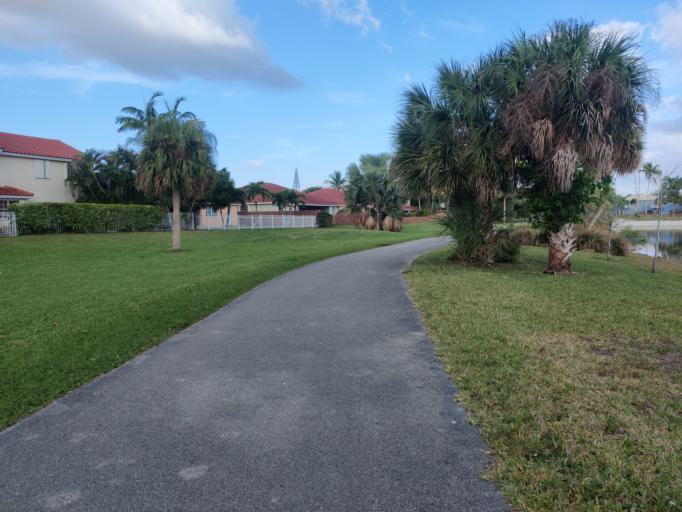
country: US
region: Florida
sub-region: Miami-Dade County
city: The Hammocks
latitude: 25.6661
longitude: -80.4552
